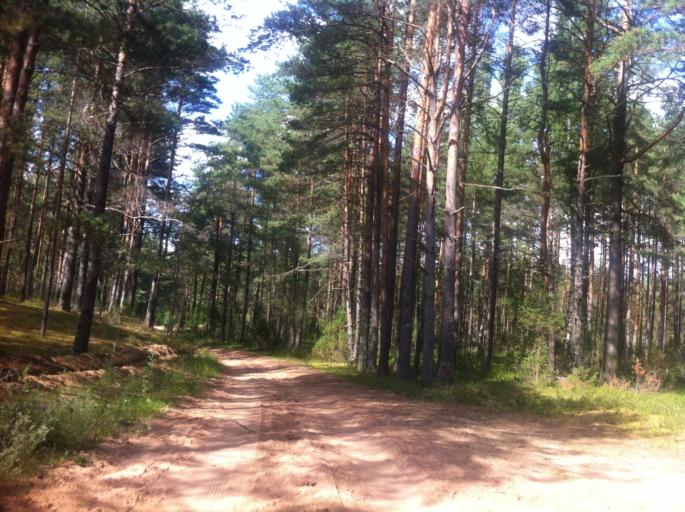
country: RU
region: Pskov
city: Izborsk
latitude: 57.8314
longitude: 27.9377
